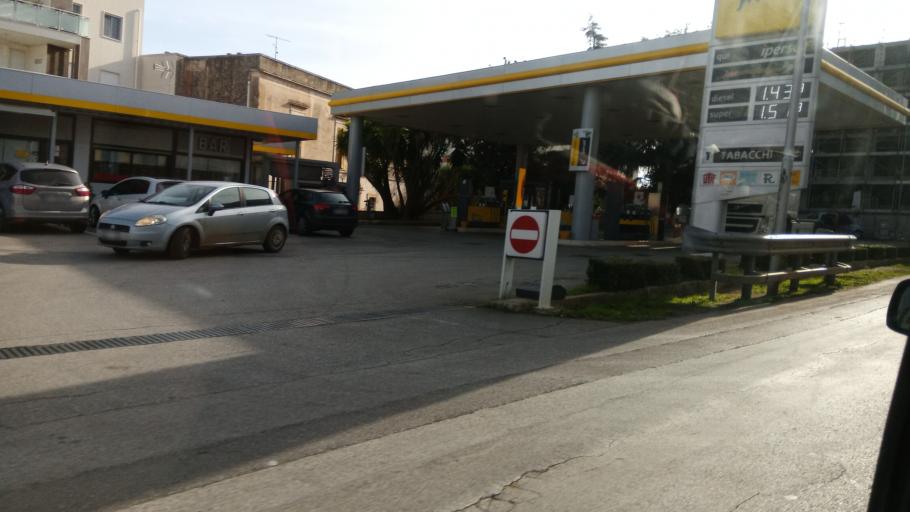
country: IT
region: Apulia
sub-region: Provincia di Bari
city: Castellana
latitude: 40.8907
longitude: 17.1665
